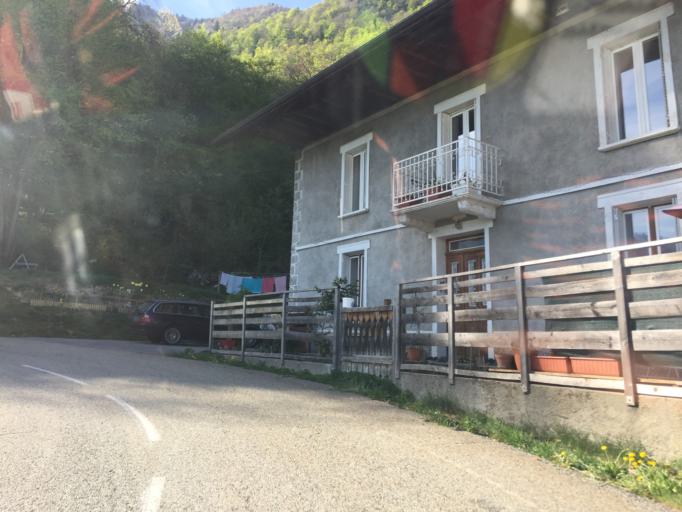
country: FR
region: Rhone-Alpes
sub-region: Departement de la Savoie
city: Mercury
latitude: 45.6667
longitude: 6.3020
